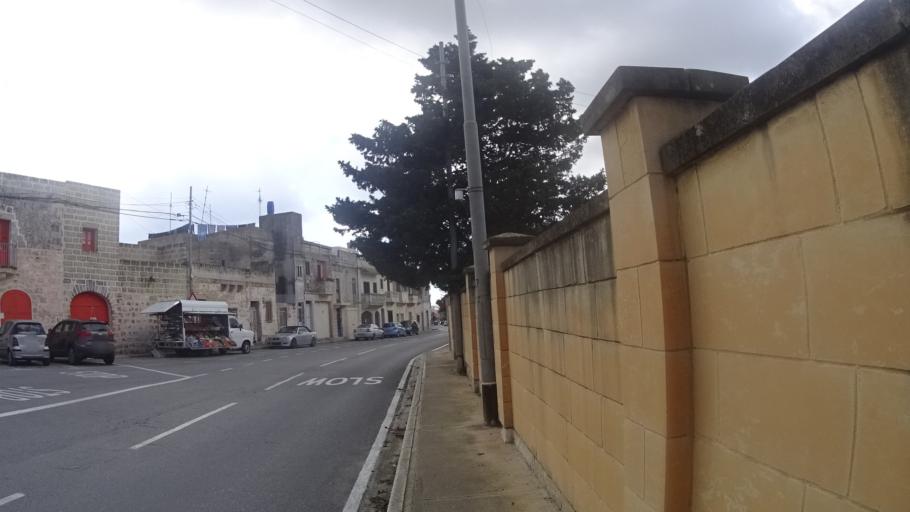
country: MT
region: L-Imtarfa
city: Imtarfa
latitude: 35.8905
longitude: 14.3972
